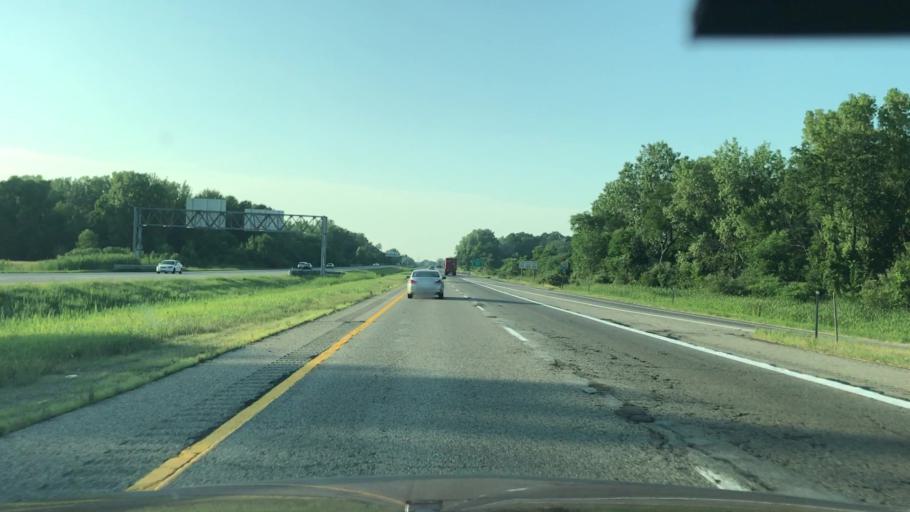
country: US
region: Michigan
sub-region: Berrien County
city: Benton Heights
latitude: 42.1390
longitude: -86.3681
